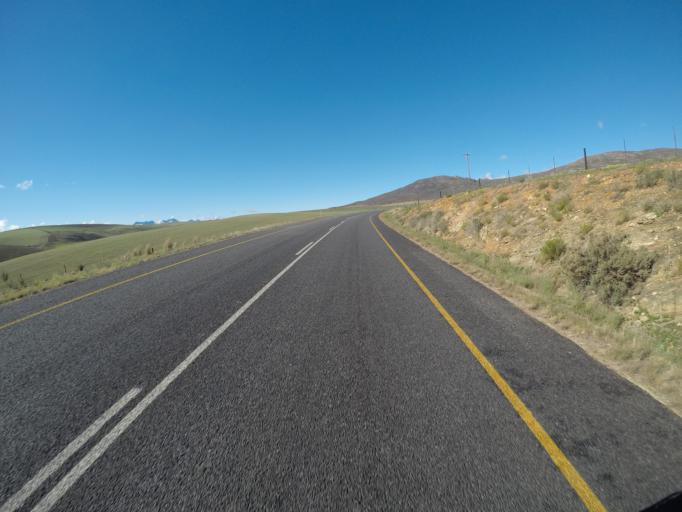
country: ZA
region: Western Cape
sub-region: Overberg District Municipality
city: Caledon
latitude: -34.1548
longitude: 19.4625
